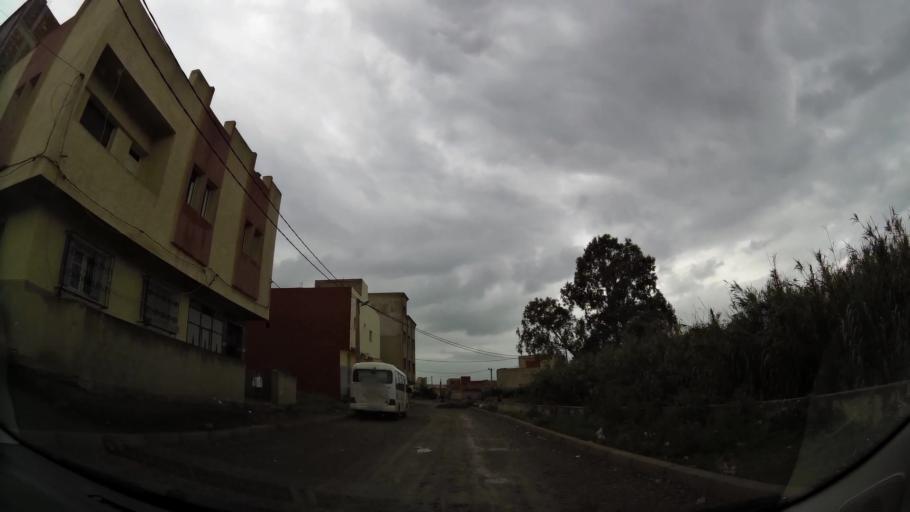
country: MA
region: Oriental
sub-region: Nador
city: Nador
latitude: 35.1487
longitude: -2.9846
